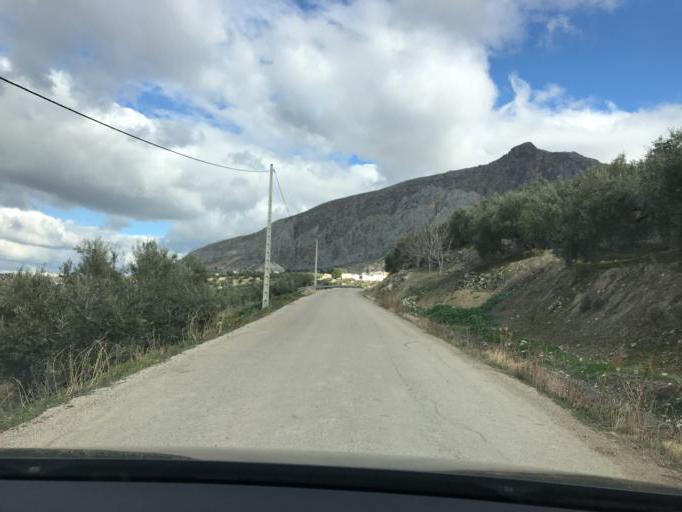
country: ES
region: Andalusia
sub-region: Provincia de Jaen
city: Jimena
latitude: 37.8173
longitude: -3.4224
